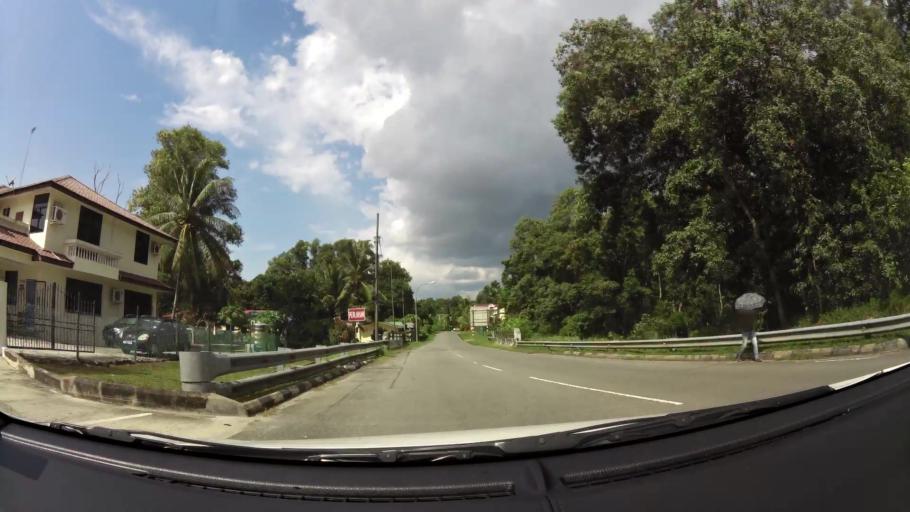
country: BN
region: Brunei and Muara
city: Bandar Seri Begawan
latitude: 4.9545
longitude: 114.9478
